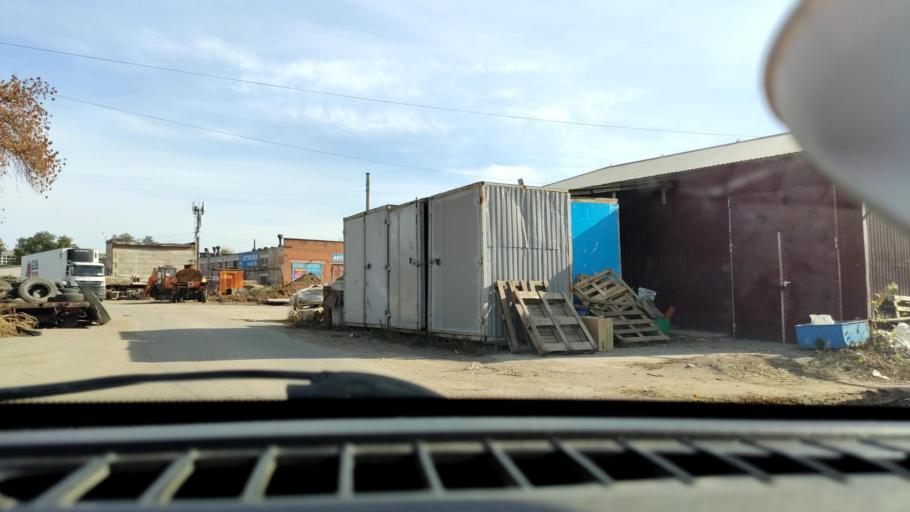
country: RU
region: Samara
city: Samara
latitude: 53.1965
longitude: 50.2556
